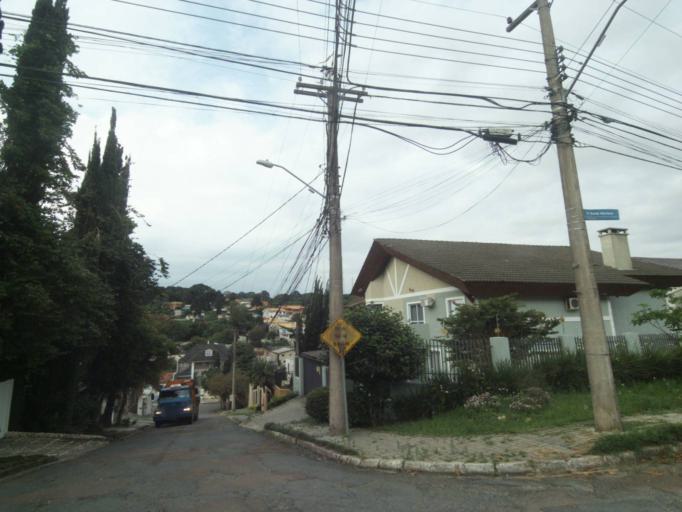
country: BR
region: Parana
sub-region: Curitiba
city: Curitiba
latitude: -25.3998
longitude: -49.2812
